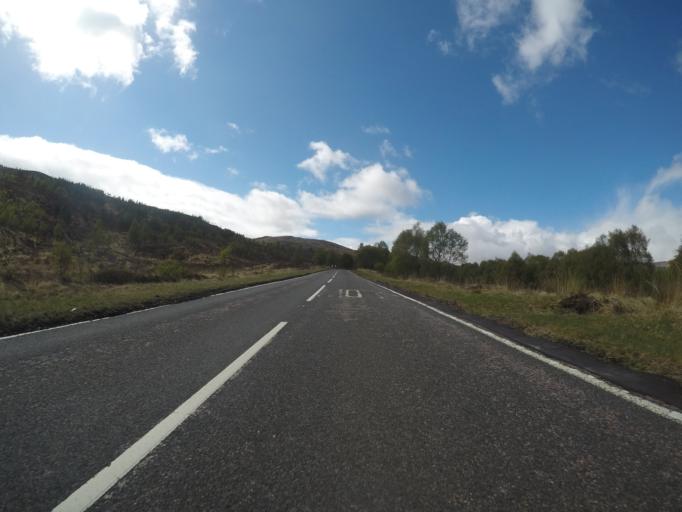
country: GB
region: Scotland
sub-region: Highland
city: Spean Bridge
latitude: 57.1273
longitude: -4.9648
